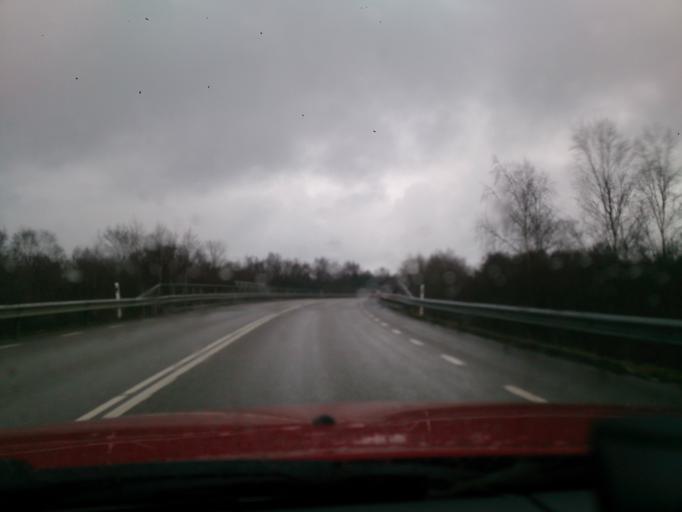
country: SE
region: Skane
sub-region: Ystads Kommun
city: Ystad
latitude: 55.4276
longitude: 13.7723
